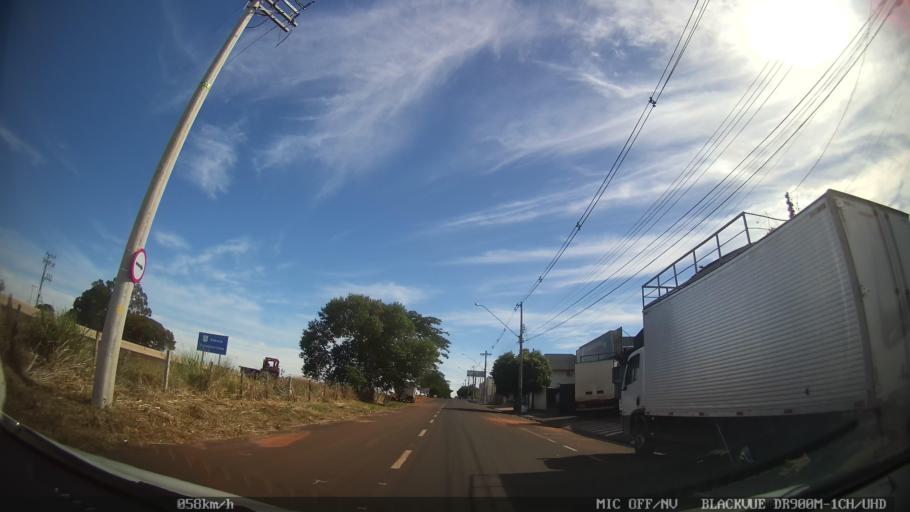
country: BR
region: Sao Paulo
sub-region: Sao Jose Do Rio Preto
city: Sao Jose do Rio Preto
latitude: -20.8502
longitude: -49.3816
